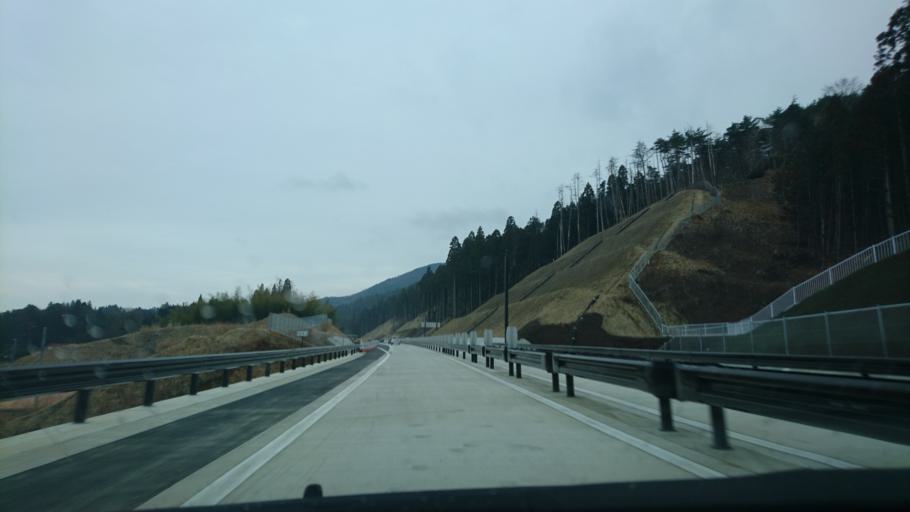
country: JP
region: Iwate
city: Ofunato
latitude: 38.9635
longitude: 141.6243
